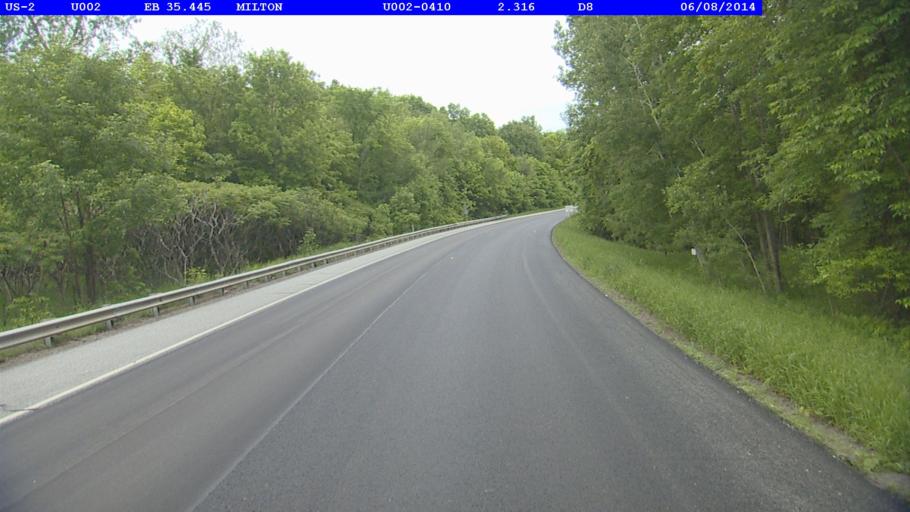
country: US
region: Vermont
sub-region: Chittenden County
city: Colchester
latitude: 44.6218
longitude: -73.2120
